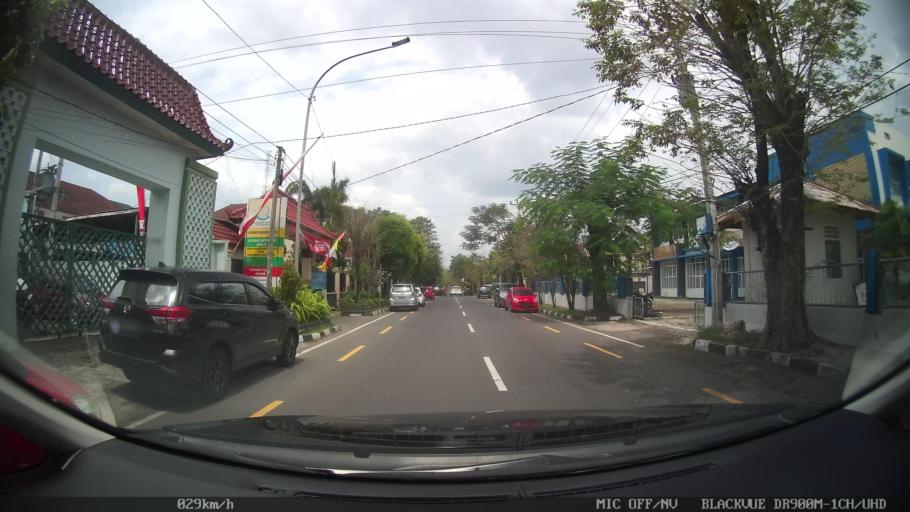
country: ID
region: Daerah Istimewa Yogyakarta
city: Yogyakarta
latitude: -7.7986
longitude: 110.3817
